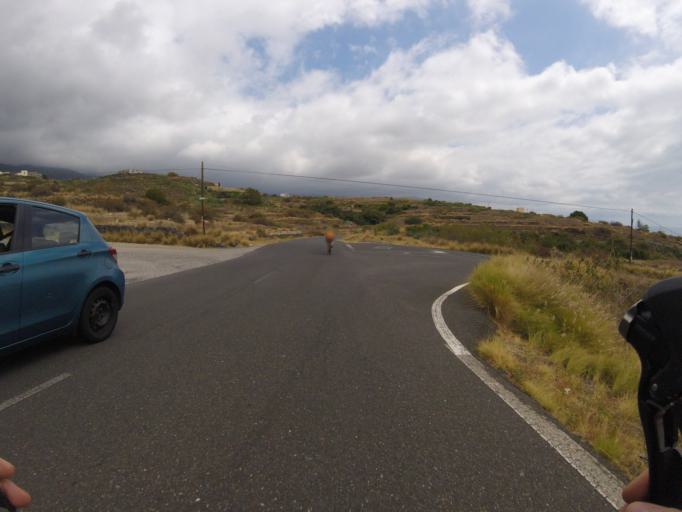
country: ES
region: Canary Islands
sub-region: Provincia de Santa Cruz de Tenerife
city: Guimar
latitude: 28.3052
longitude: -16.4163
